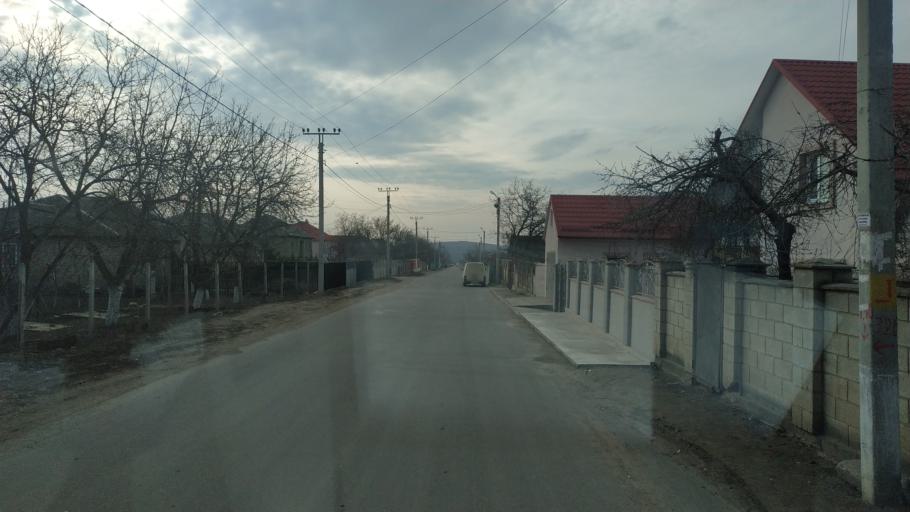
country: MD
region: Chisinau
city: Singera
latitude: 46.9661
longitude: 29.0655
